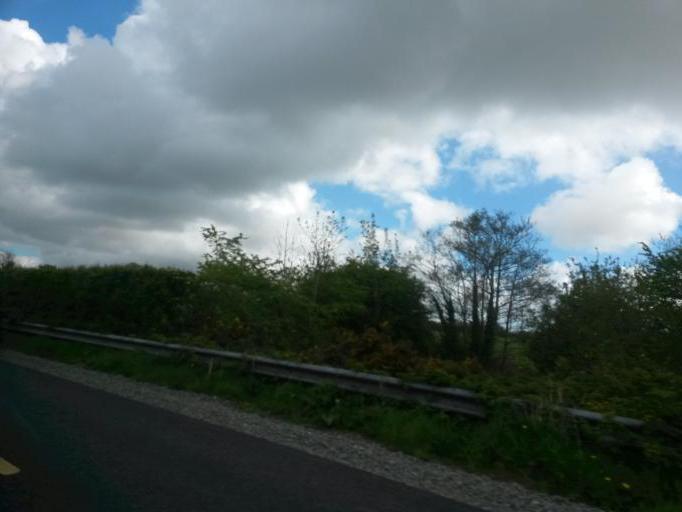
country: IE
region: Leinster
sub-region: Loch Garman
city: Castlebridge
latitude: 52.4112
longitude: -6.5223
